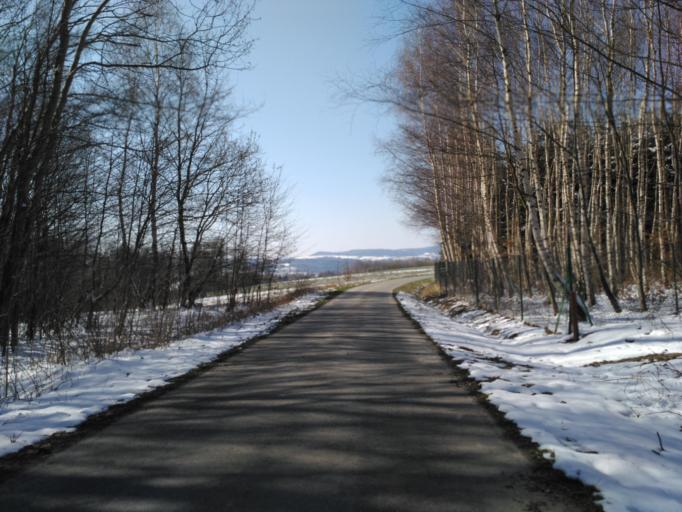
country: PL
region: Subcarpathian Voivodeship
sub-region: Powiat ropczycko-sedziszowski
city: Wielopole Skrzynskie
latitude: 49.9730
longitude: 21.6044
